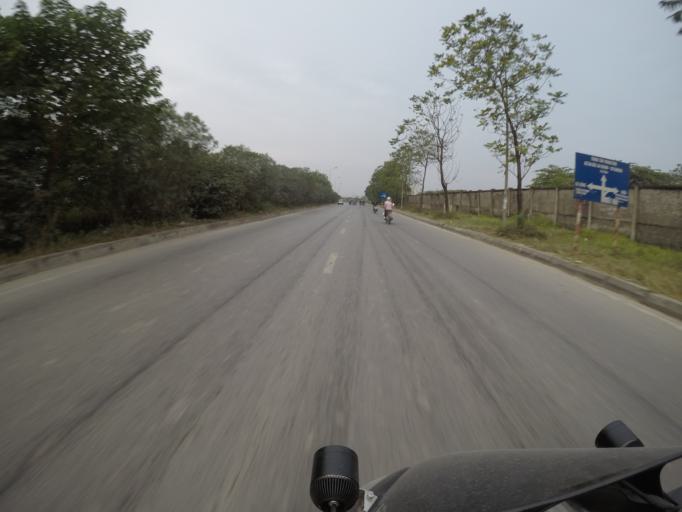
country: VN
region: Ha Noi
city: Cau Dien
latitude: 21.0092
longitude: 105.7520
